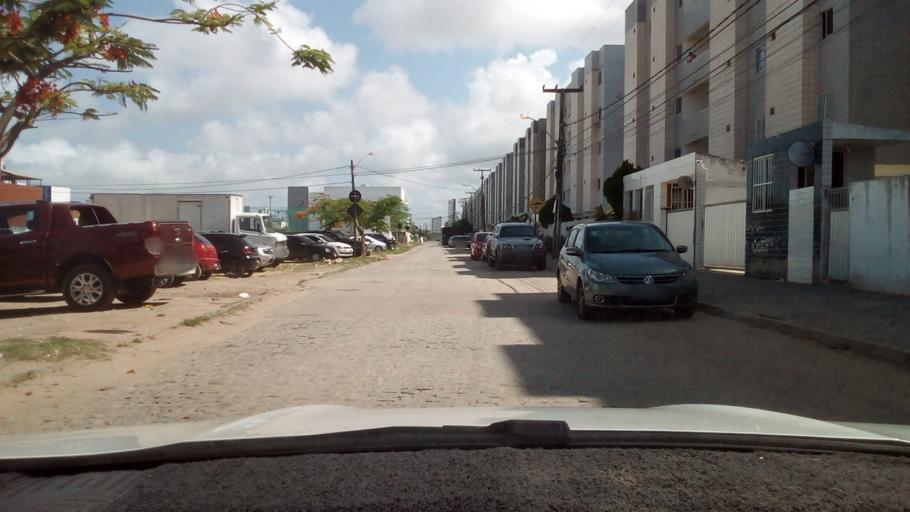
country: BR
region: Paraiba
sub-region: Joao Pessoa
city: Joao Pessoa
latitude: -7.0814
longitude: -34.8462
